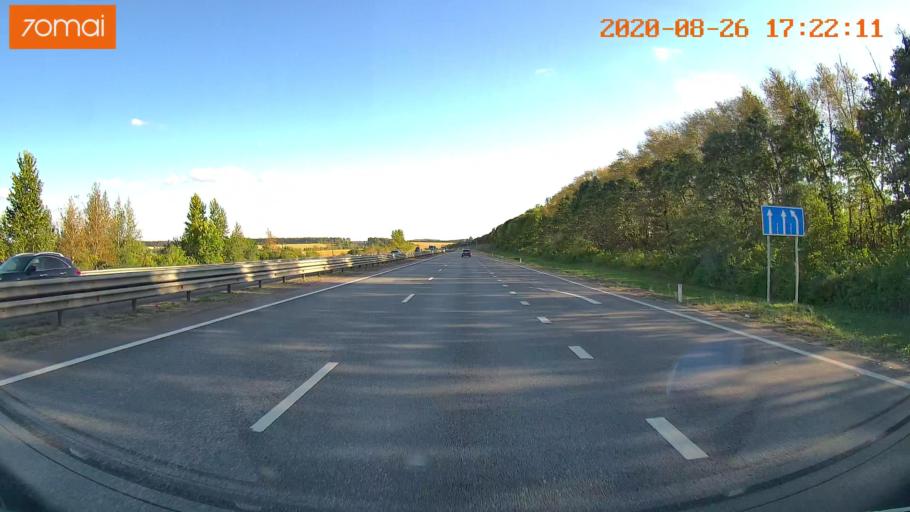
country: RU
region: Tula
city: Volovo
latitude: 53.5536
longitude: 38.1124
